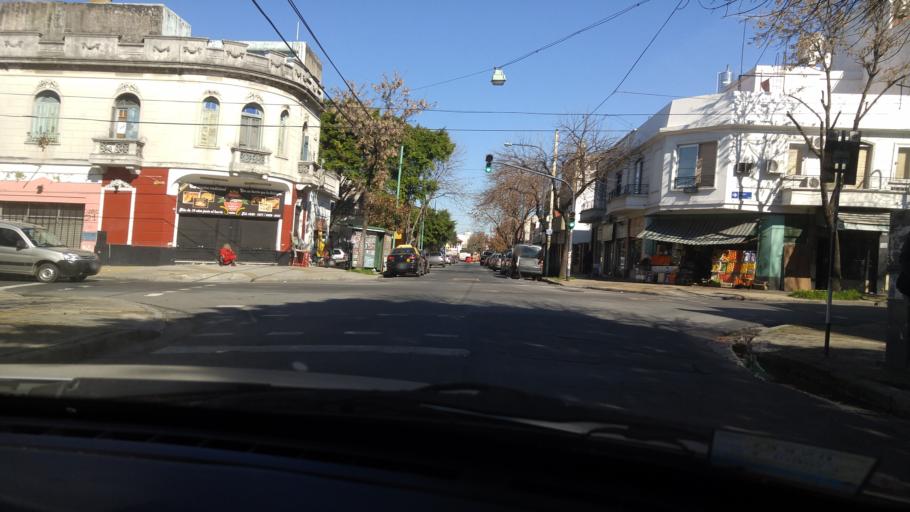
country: AR
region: Buenos Aires F.D.
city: Villa Santa Rita
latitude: -34.6230
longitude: -58.4938
